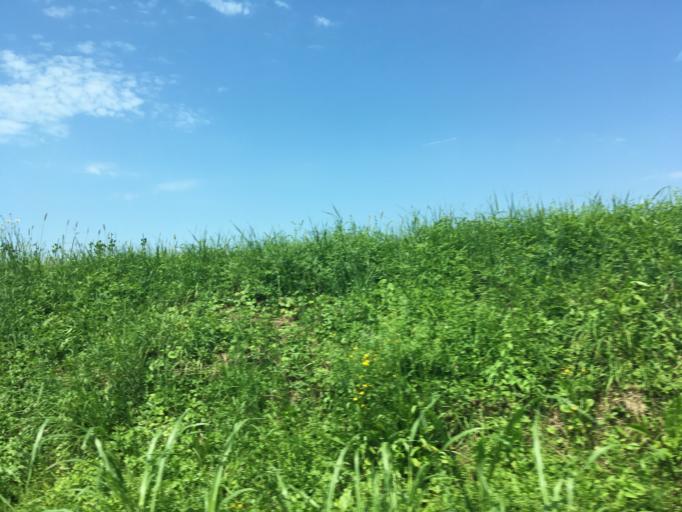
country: SI
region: Metlika
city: Metlika
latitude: 45.6471
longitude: 15.3451
